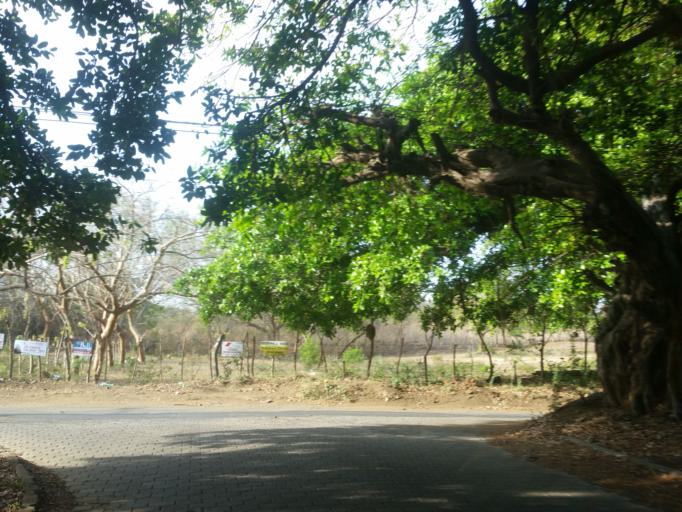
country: NI
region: Managua
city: Managua
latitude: 12.0782
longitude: -86.2502
